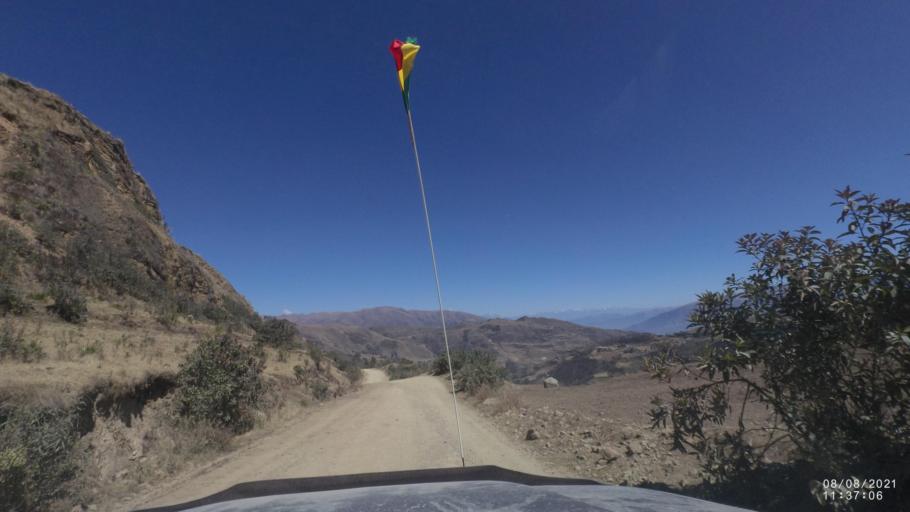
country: BO
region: Cochabamba
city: Colchani
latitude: -16.7839
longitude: -66.6462
